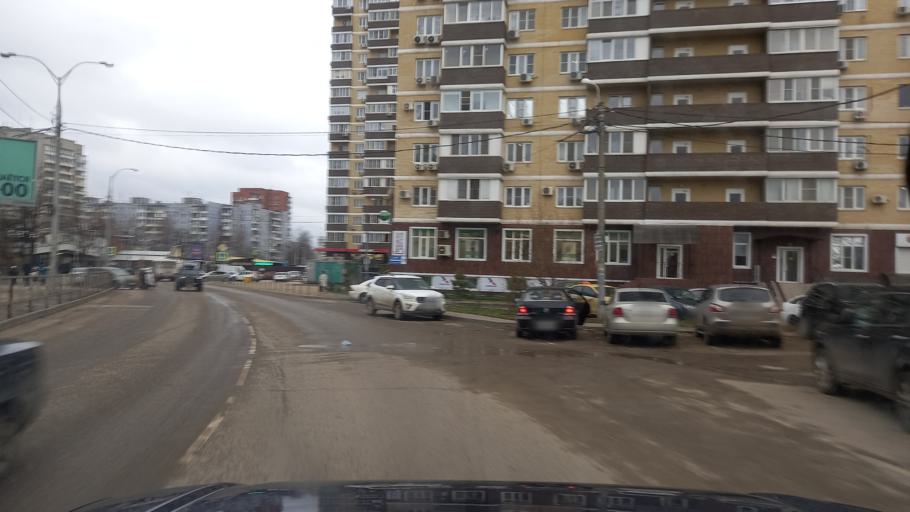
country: RU
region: Krasnodarskiy
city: Pashkovskiy
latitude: 45.0407
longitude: 39.0975
